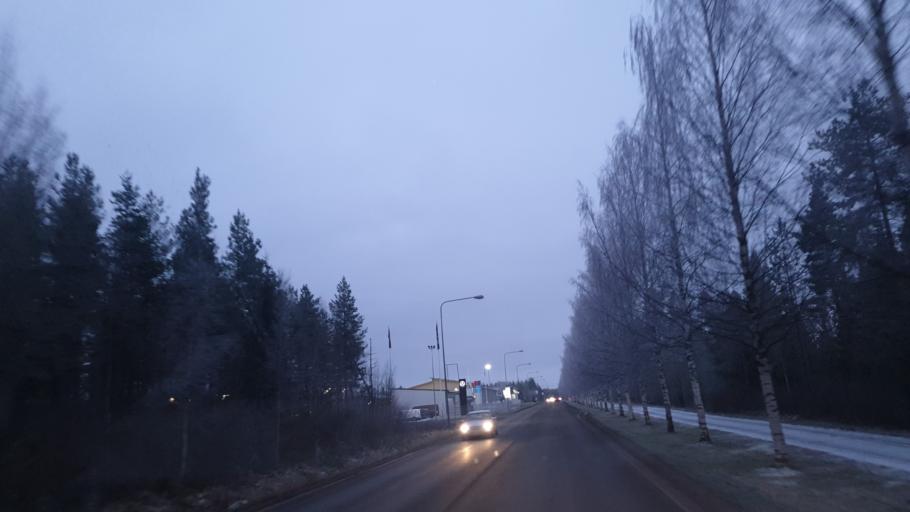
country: FI
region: Southern Ostrobothnia
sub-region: Seinaejoki
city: Nurmo
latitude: 62.7852
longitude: 22.9016
